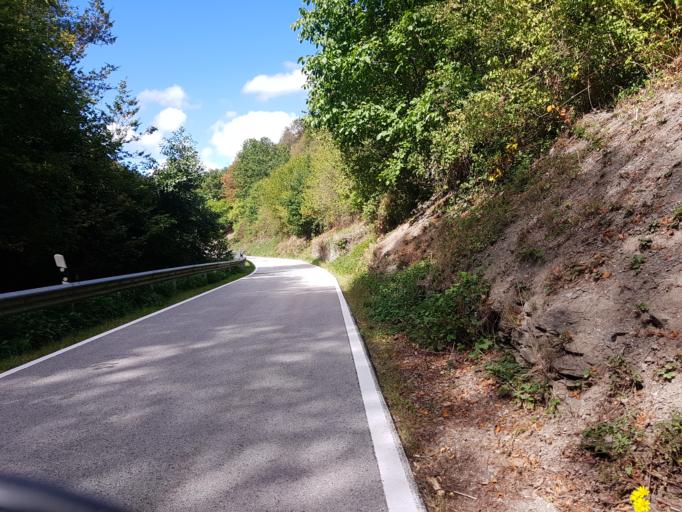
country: DE
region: Rheinland-Pfalz
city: Manubach
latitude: 50.0585
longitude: 7.7309
